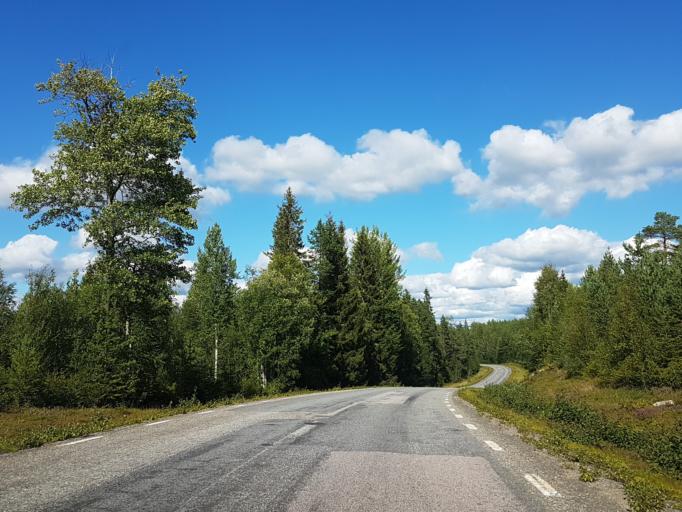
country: SE
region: Vaesterbotten
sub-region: Skelleftea Kommun
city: Burtraesk
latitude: 64.2332
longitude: 20.4737
